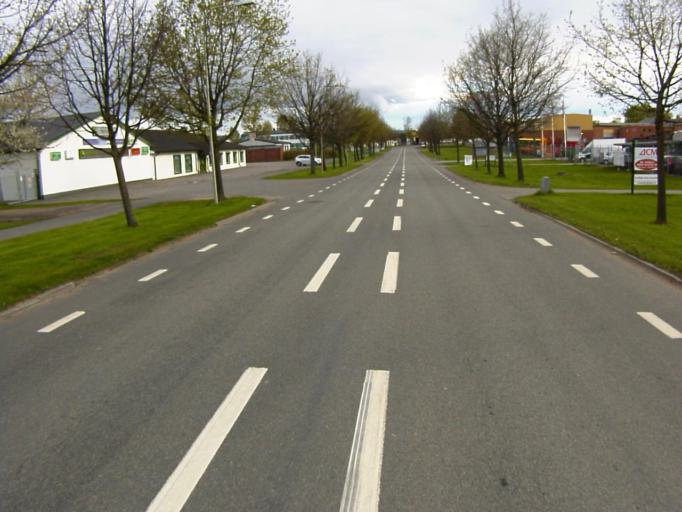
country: SE
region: Skane
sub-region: Kristianstads Kommun
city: Kristianstad
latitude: 56.0459
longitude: 14.1598
